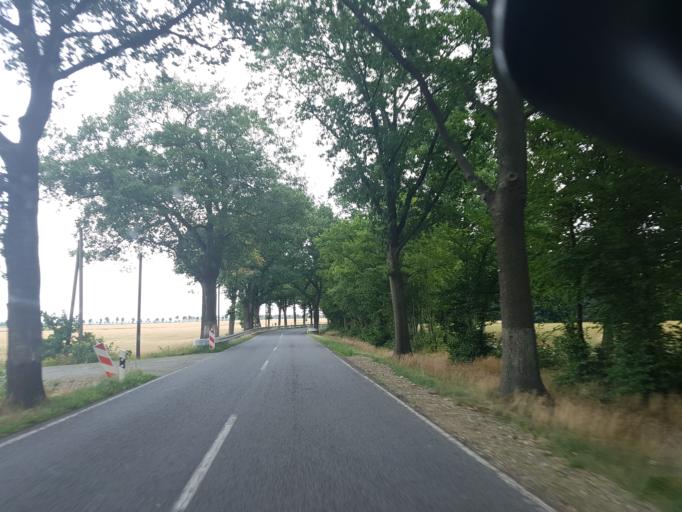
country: DE
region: Brandenburg
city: Dahme
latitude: 51.8484
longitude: 13.4108
